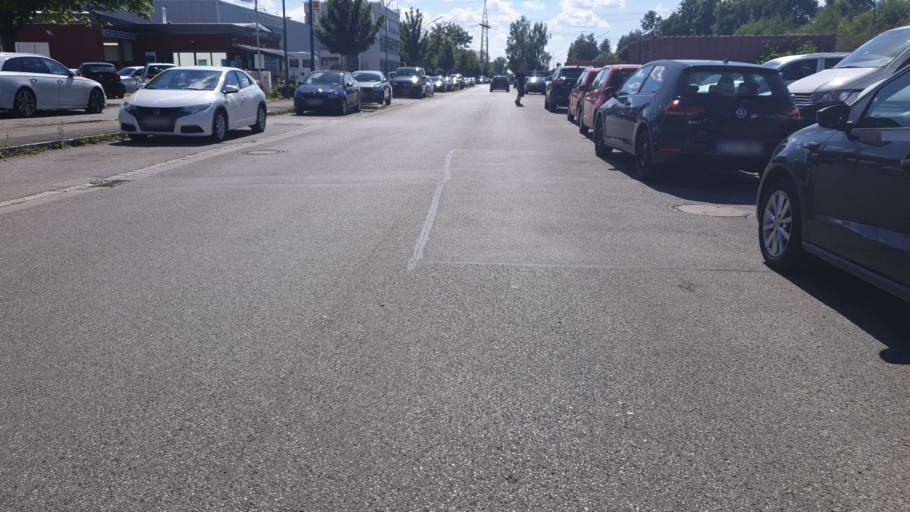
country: DE
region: Bavaria
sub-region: Upper Bavaria
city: Puchheim
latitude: 48.1691
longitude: 11.3645
